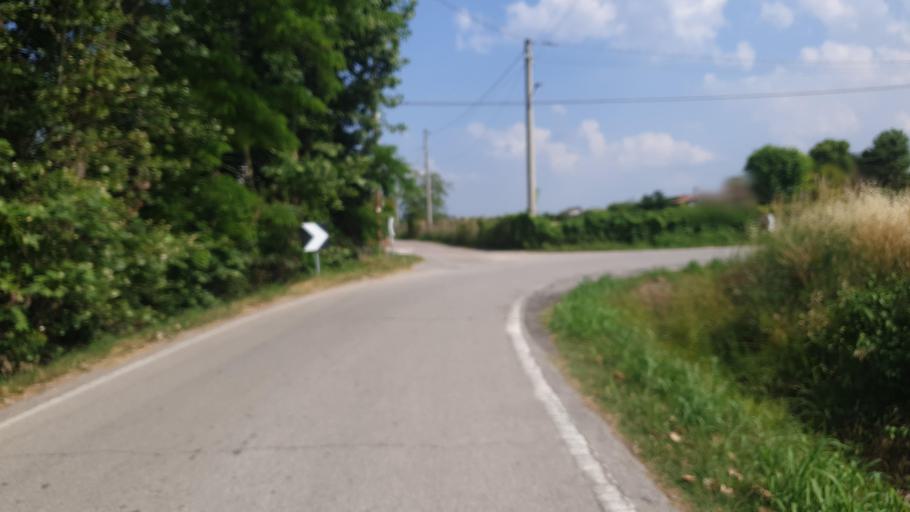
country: IT
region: Veneto
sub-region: Provincia di Padova
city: Tencarola
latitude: 45.3751
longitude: 11.8140
